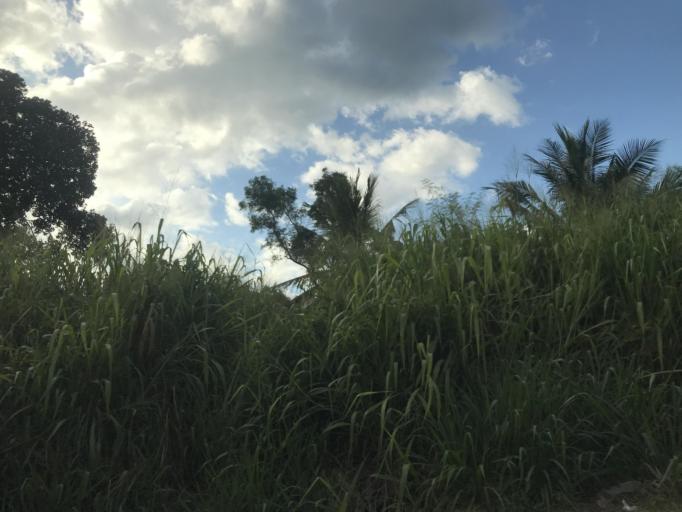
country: LK
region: Western
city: Gampaha
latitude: 7.0874
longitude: 79.9894
